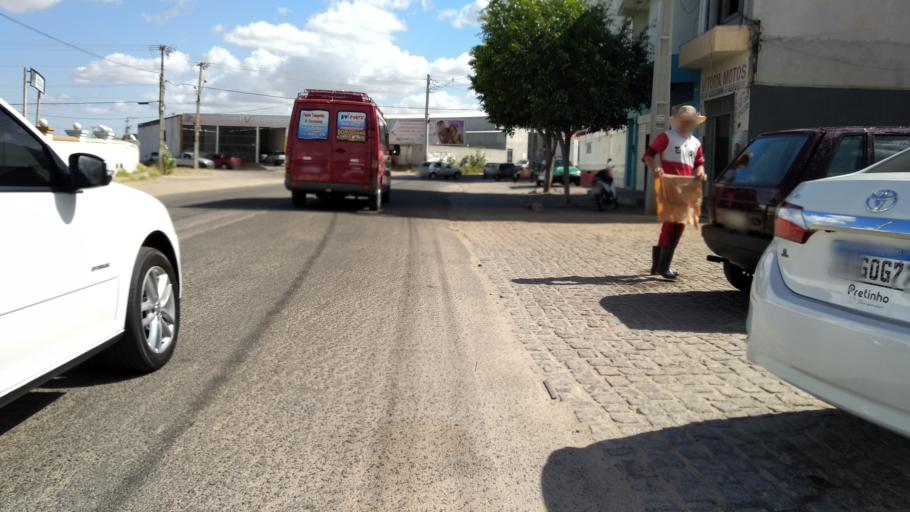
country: BR
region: Bahia
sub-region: Guanambi
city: Guanambi
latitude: -14.2322
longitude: -42.7800
